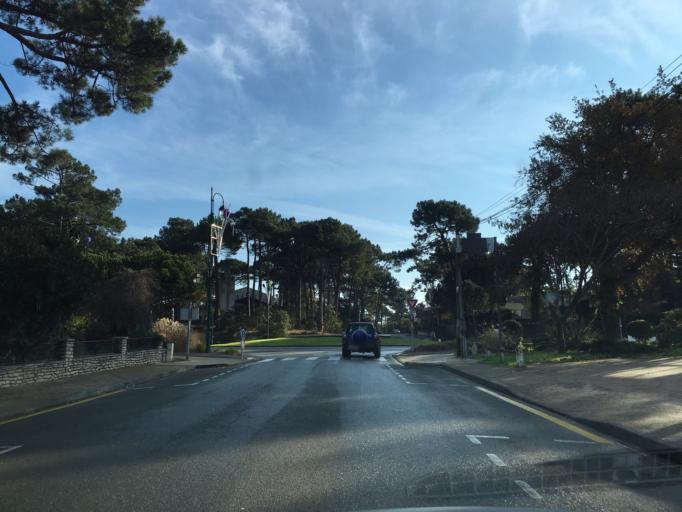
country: FR
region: Aquitaine
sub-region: Departement de la Gironde
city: Arcachon
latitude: 44.6479
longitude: -1.1846
